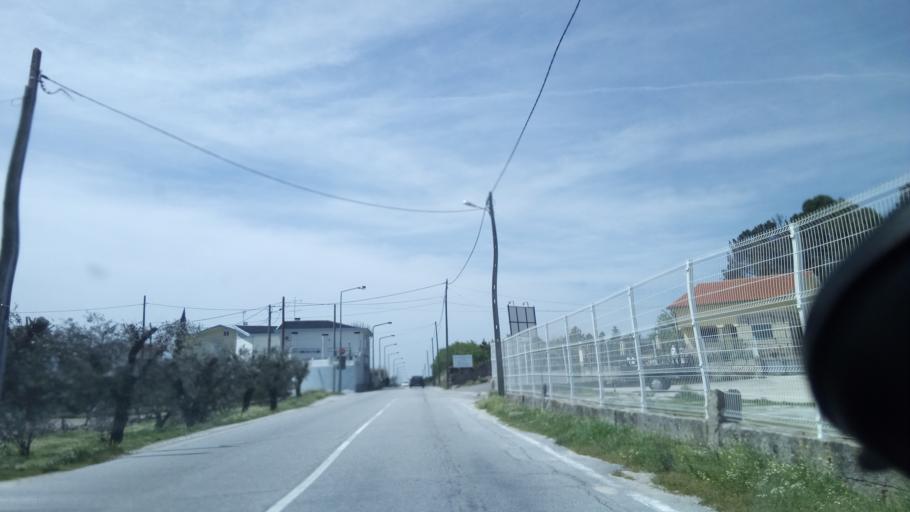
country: PT
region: Viseu
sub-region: Mangualde
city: Mangualde
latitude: 40.6062
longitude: -7.7425
